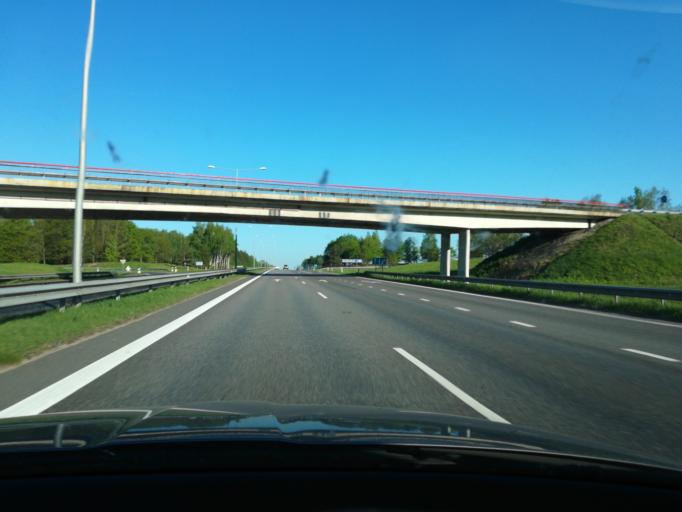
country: LT
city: Ziezmariai
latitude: 54.8182
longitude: 24.4280
